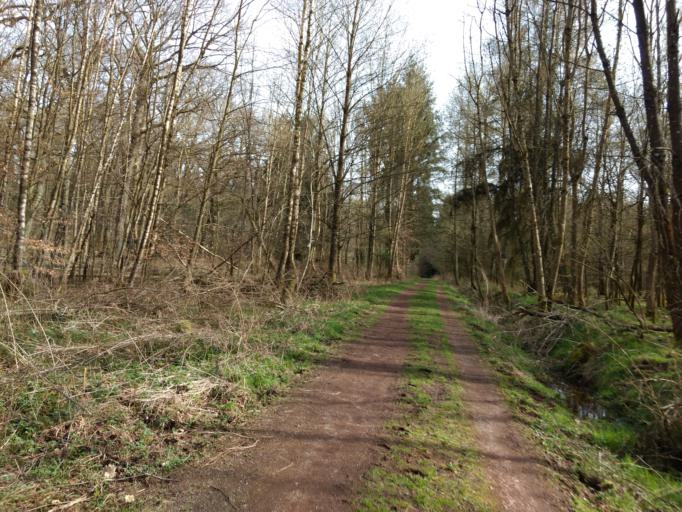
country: DE
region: Saarland
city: Dillingen
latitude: 49.3710
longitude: 6.7442
